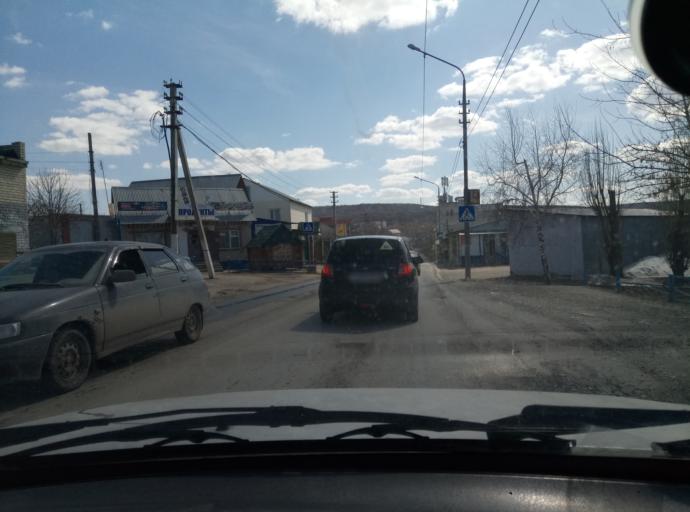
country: RU
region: Saratov
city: Sokolovyy
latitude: 51.5775
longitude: 45.8995
